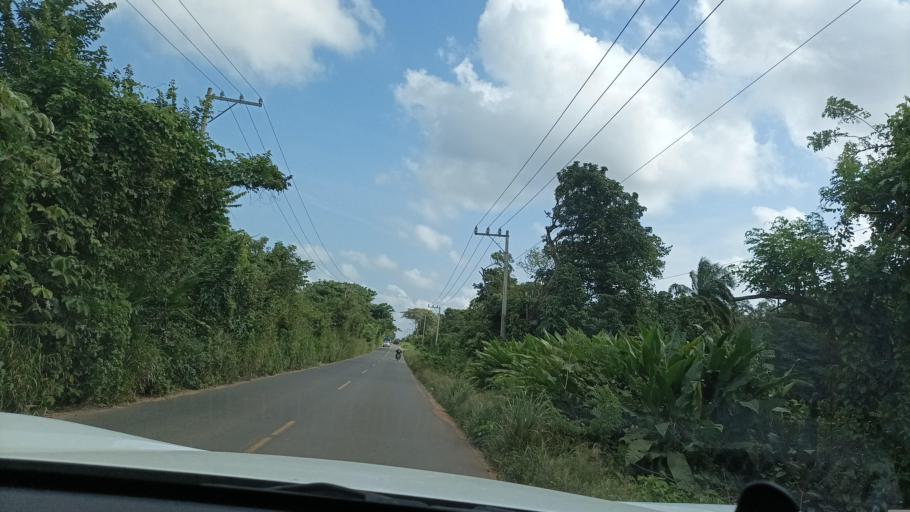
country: MX
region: Veracruz
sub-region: Chinameca
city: Chacalapa
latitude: 18.0734
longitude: -94.6936
